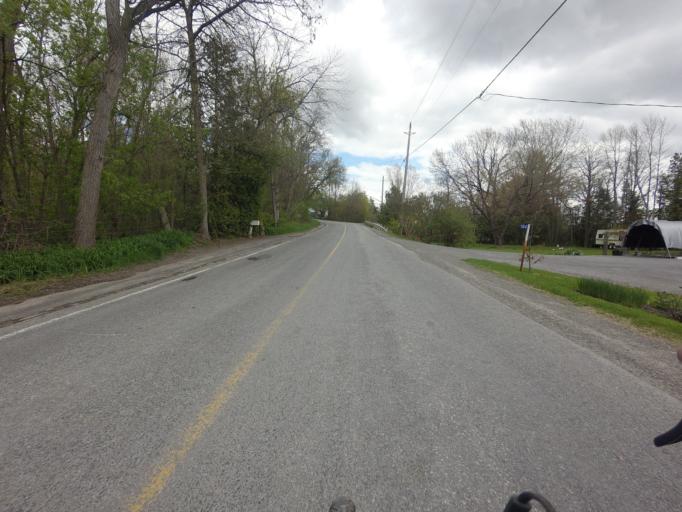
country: CA
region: Ontario
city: Carleton Place
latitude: 45.2655
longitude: -76.2478
